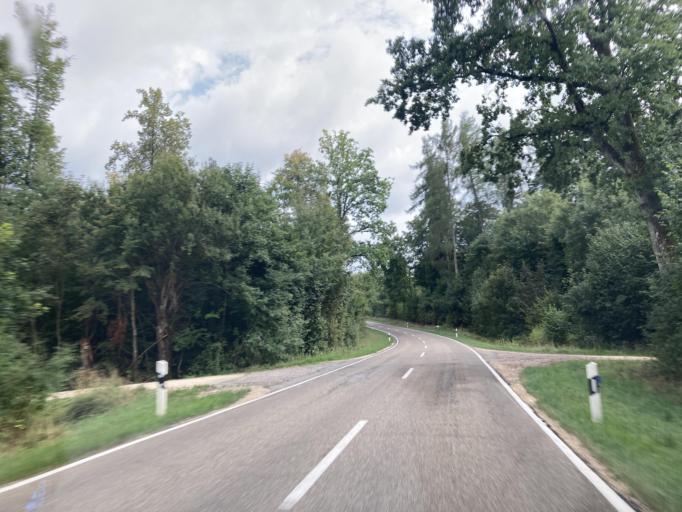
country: DE
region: Bavaria
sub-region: Swabia
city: Medlingen
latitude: 48.5925
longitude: 10.3091
